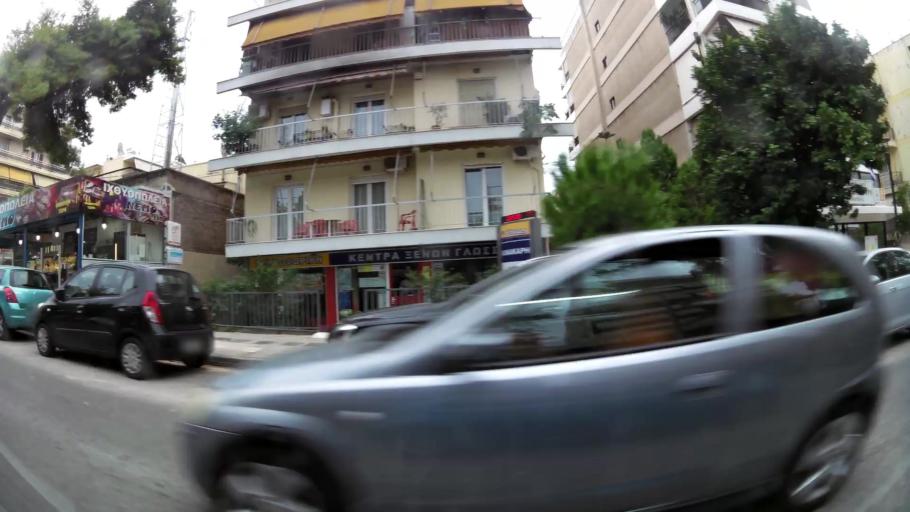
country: GR
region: Attica
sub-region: Nomarchia Athinas
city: Palaio Faliro
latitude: 37.9222
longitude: 23.7091
